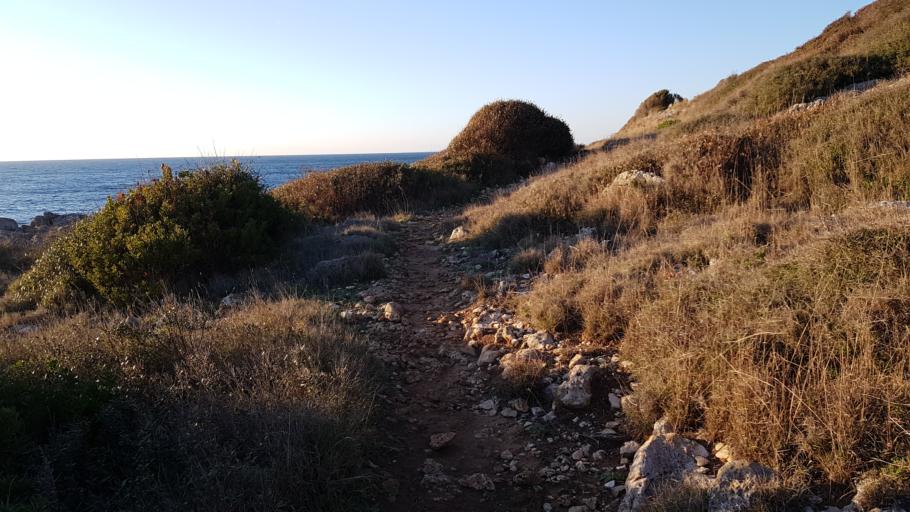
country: IT
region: Apulia
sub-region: Provincia di Lecce
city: Nardo
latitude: 40.1528
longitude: 17.9615
